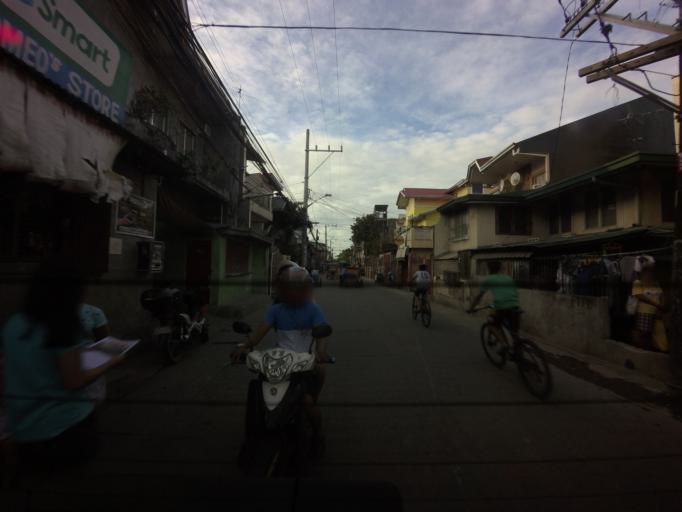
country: PH
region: Central Luzon
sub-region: Province of Bulacan
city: Obando
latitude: 14.7274
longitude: 120.9245
